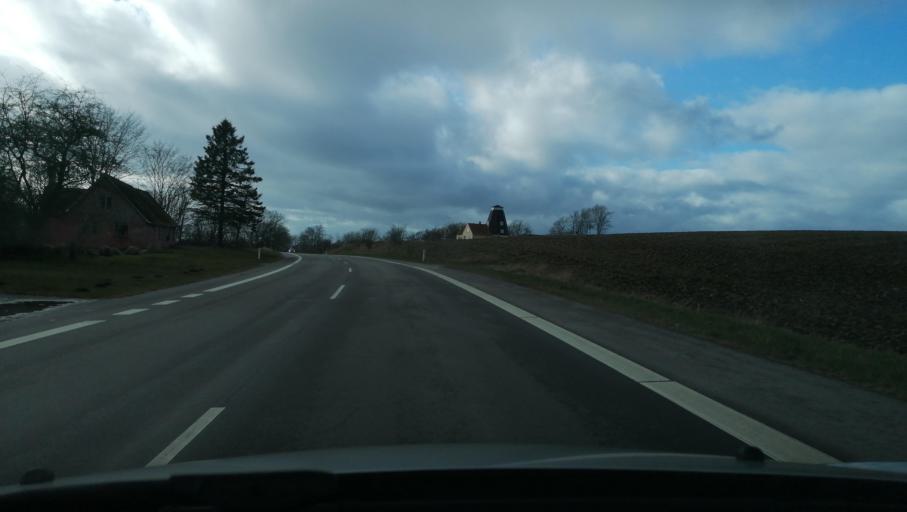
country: DK
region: Zealand
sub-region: Odsherred Kommune
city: Horve
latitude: 55.7642
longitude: 11.4365
